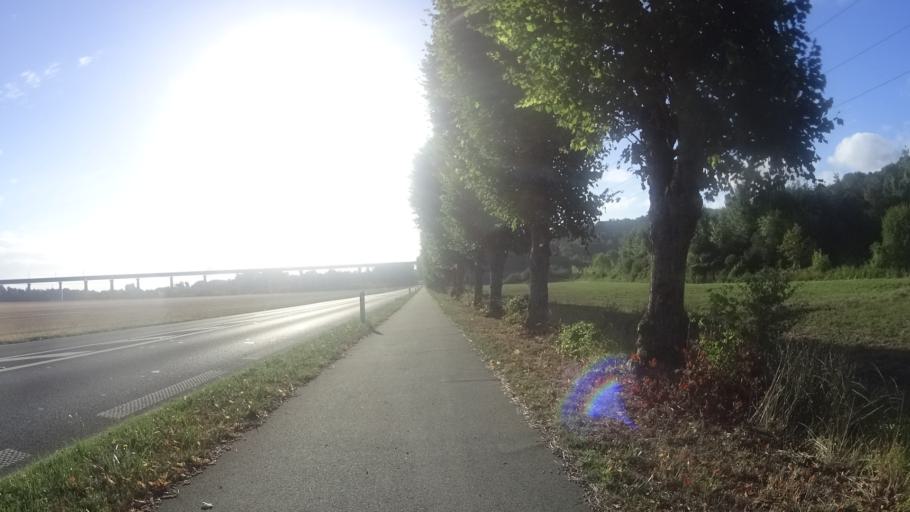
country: FR
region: Picardie
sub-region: Departement de l'Oise
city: Verberie
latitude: 49.3092
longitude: 2.7019
